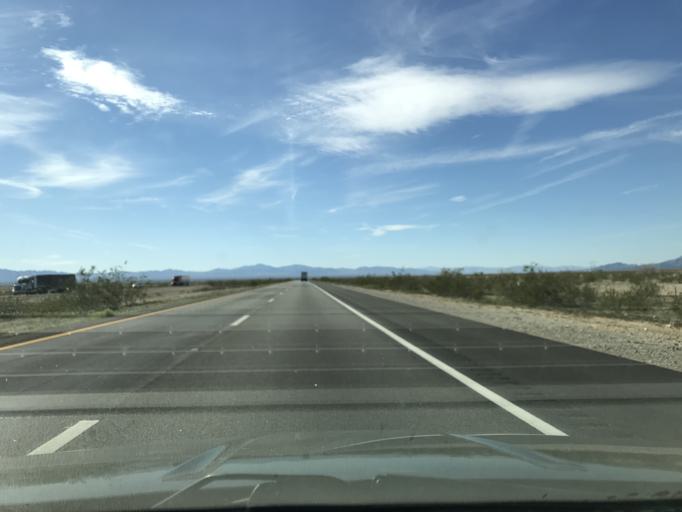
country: US
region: California
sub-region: Riverside County
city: Mesa Verde
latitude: 33.6097
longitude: -114.8552
